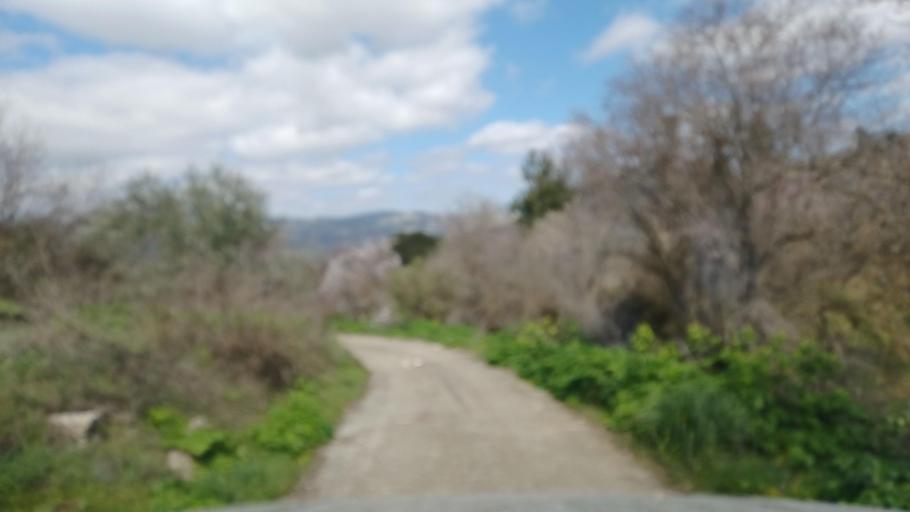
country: CY
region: Limassol
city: Pachna
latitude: 34.8277
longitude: 32.7318
